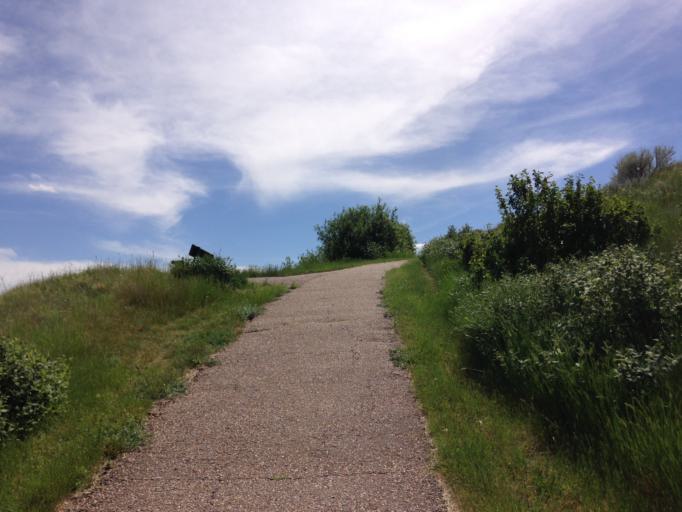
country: CA
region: Alberta
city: Medicine Hat
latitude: 50.0144
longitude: -110.6220
